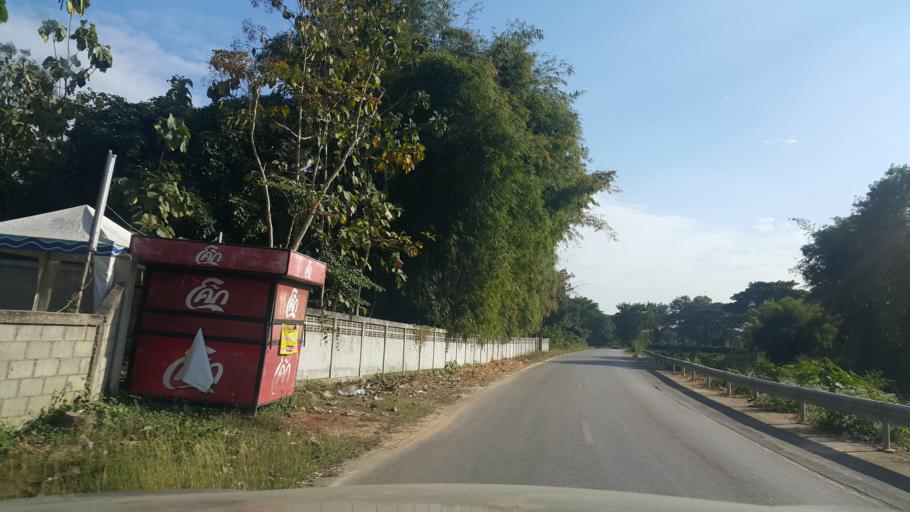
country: TH
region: Lampang
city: Hang Chat
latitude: 18.3185
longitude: 99.3476
